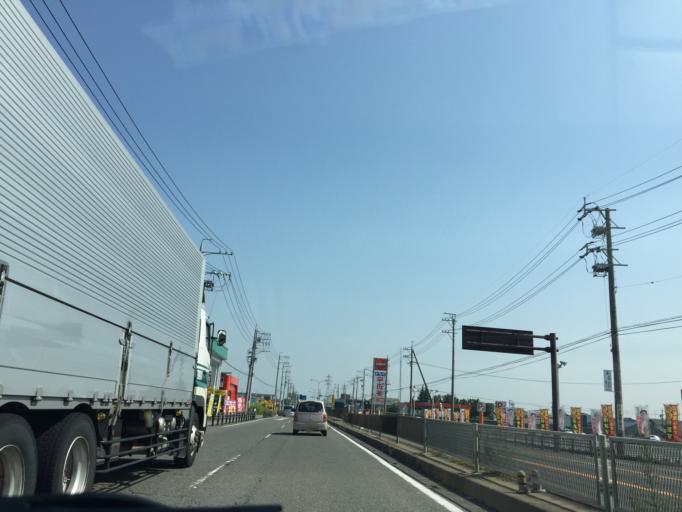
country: JP
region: Gifu
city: Ogaki
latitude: 35.3075
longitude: 136.6162
